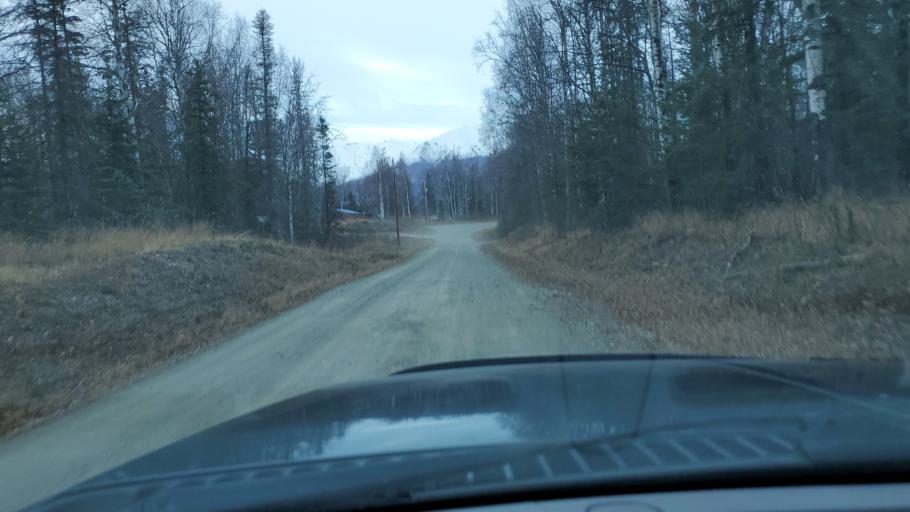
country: US
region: Alaska
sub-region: Matanuska-Susitna Borough
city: Lakes
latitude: 61.6574
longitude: -149.3036
